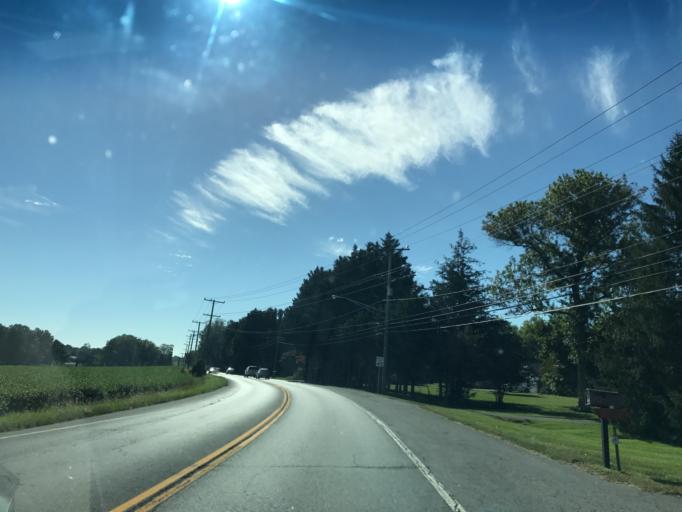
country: US
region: Maryland
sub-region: Anne Arundel County
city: Davidsonville
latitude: 38.9381
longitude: -76.6429
